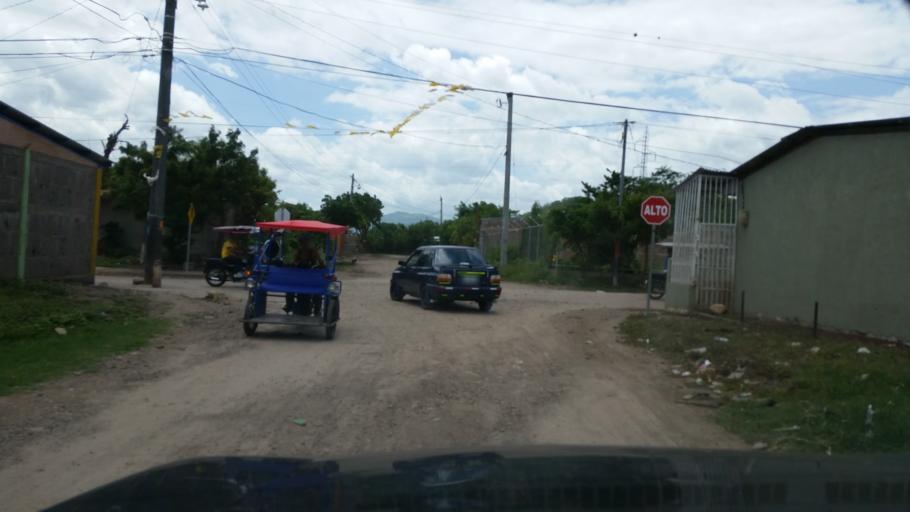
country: NI
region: Matagalpa
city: Ciudad Dario
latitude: 12.8626
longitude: -86.0907
